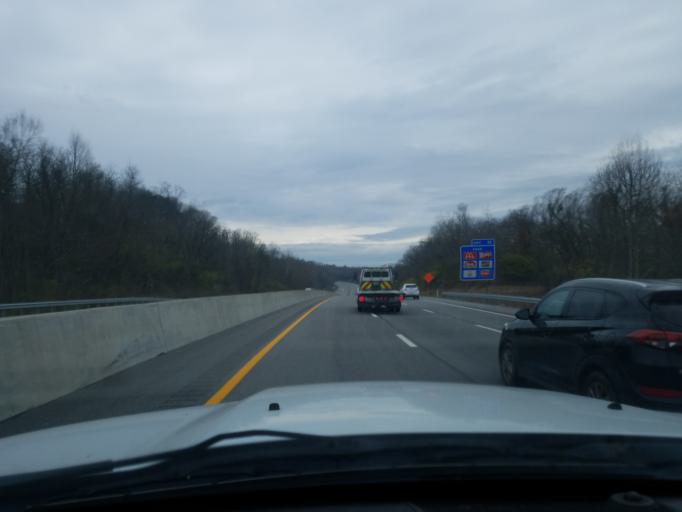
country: US
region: West Virginia
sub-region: Cabell County
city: Pea Ridge
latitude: 38.3991
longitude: -82.3827
